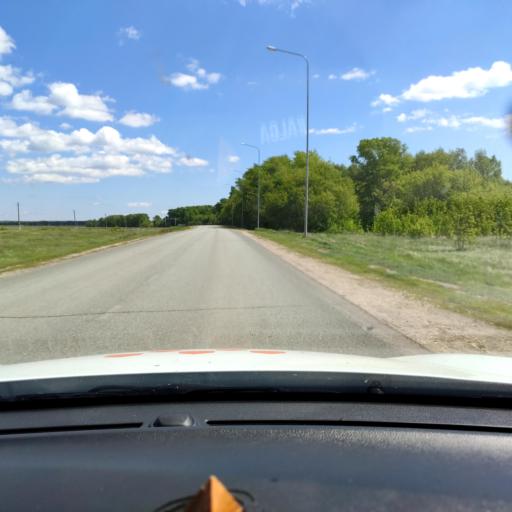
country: RU
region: Tatarstan
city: Kuybyshevskiy Zaton
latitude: 55.1603
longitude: 49.1856
